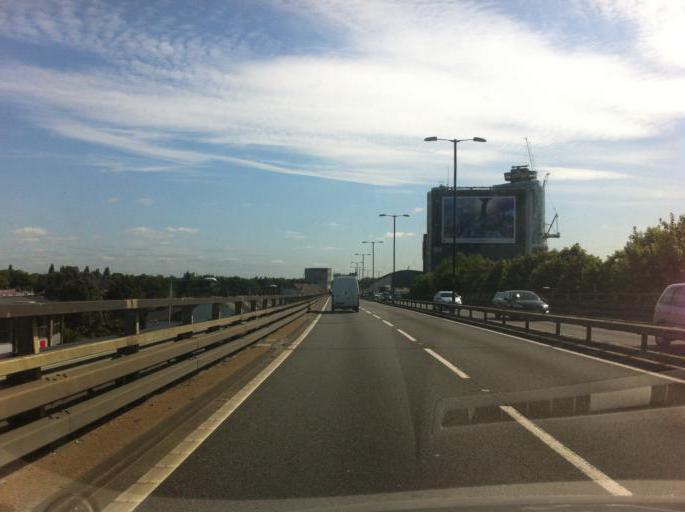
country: GB
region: England
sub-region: Greater London
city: Brentford
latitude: 51.4896
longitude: -0.3094
